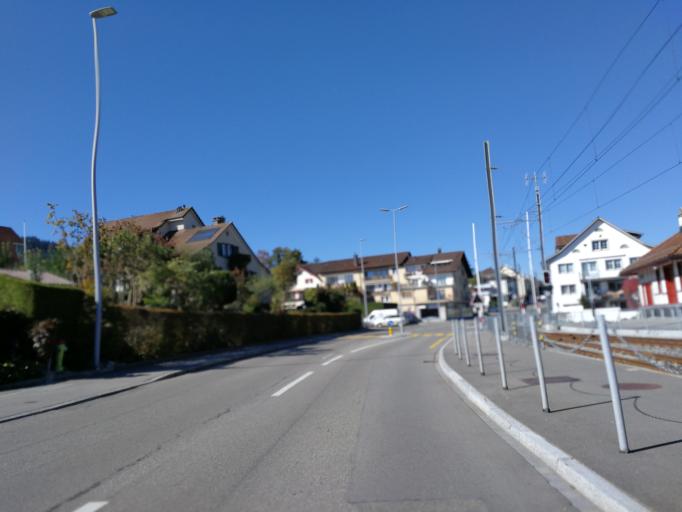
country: CH
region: Zurich
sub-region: Bezirk Uster
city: Hinteregg
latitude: 47.3058
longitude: 8.6841
